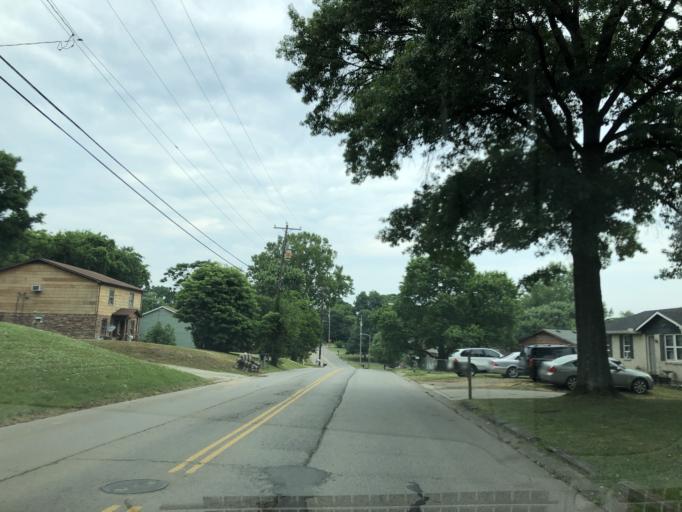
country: US
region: Tennessee
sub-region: Davidson County
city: Oak Hill
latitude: 36.0748
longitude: -86.6897
